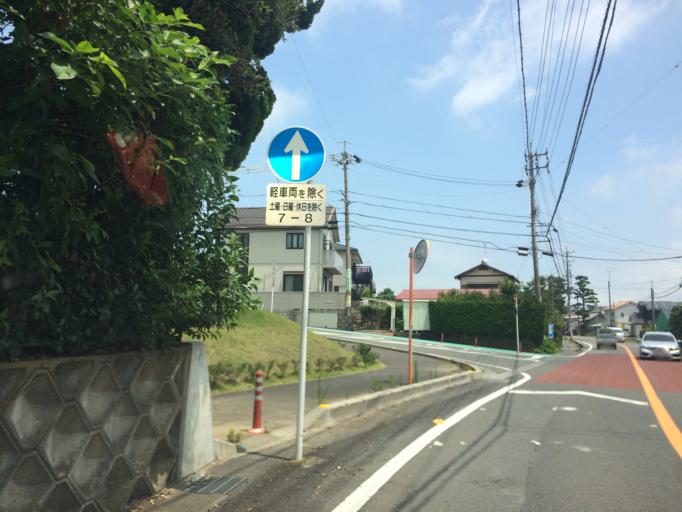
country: JP
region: Shizuoka
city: Fujieda
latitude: 34.8460
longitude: 138.2362
